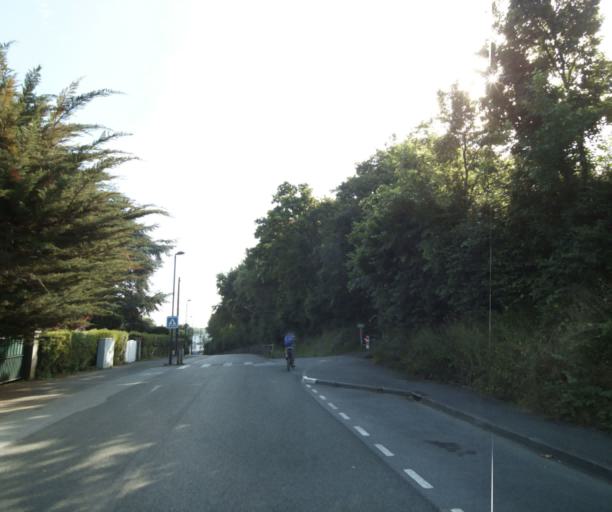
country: FR
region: Pays de la Loire
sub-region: Departement de la Mayenne
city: Laval
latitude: 48.0591
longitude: -0.7850
